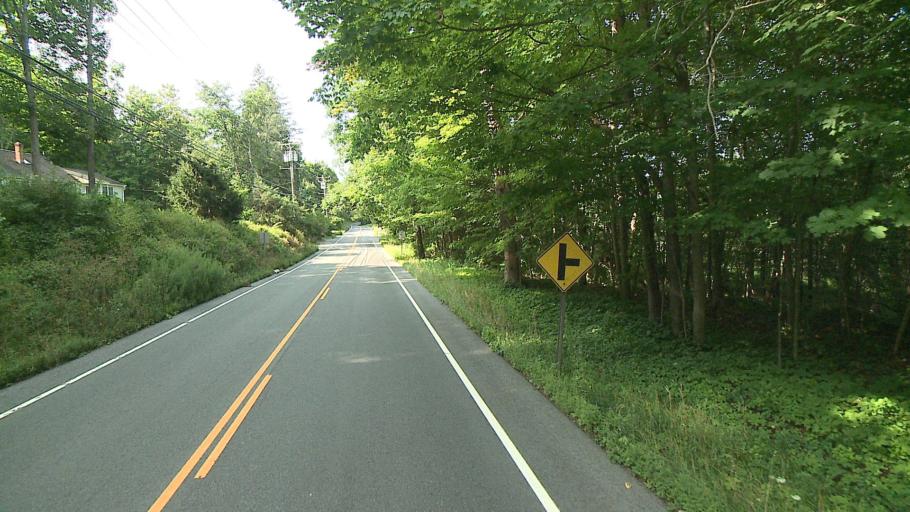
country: US
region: Connecticut
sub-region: Litchfield County
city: Kent
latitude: 41.7662
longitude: -73.4296
